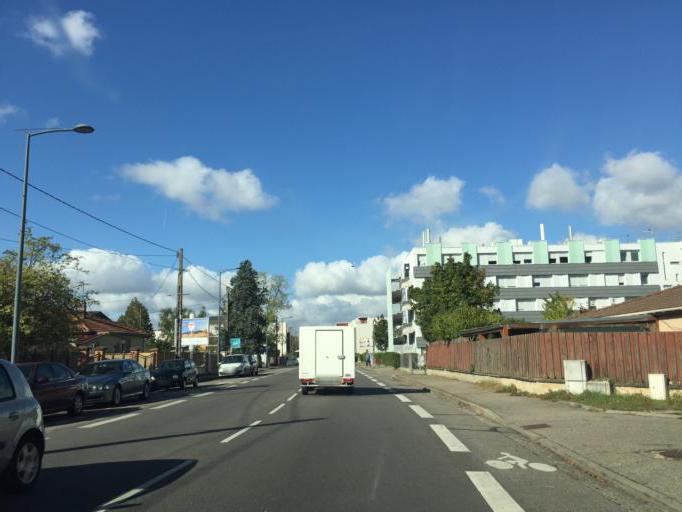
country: FR
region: Rhone-Alpes
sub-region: Departement du Rhone
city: Bron
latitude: 45.7535
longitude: 4.9316
